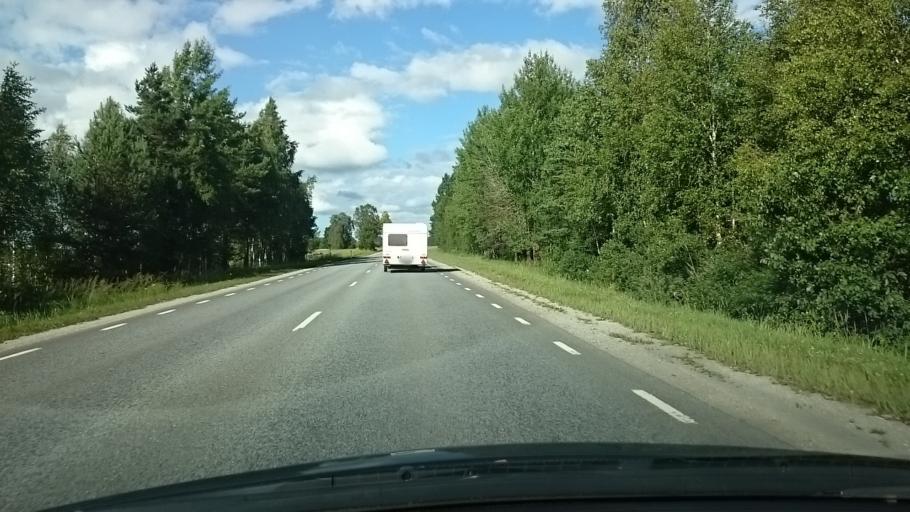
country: EE
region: Harju
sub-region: Keila linn
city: Keila
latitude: 59.2772
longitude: 24.3025
